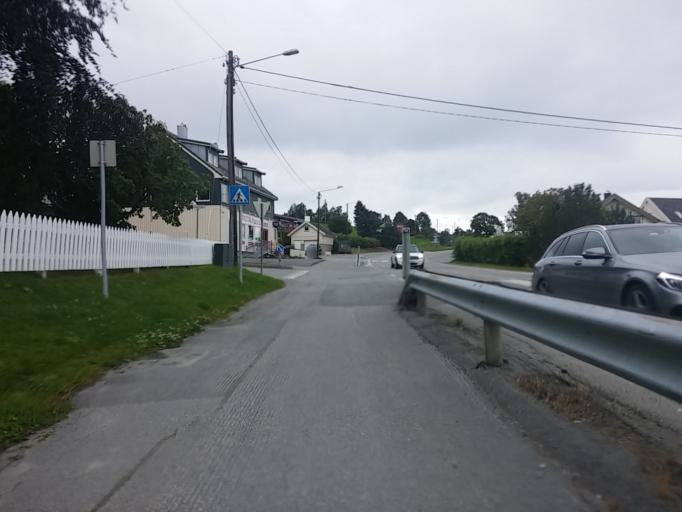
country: NO
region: Sor-Trondelag
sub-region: Malvik
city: Malvik
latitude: 63.4373
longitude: 10.6593
